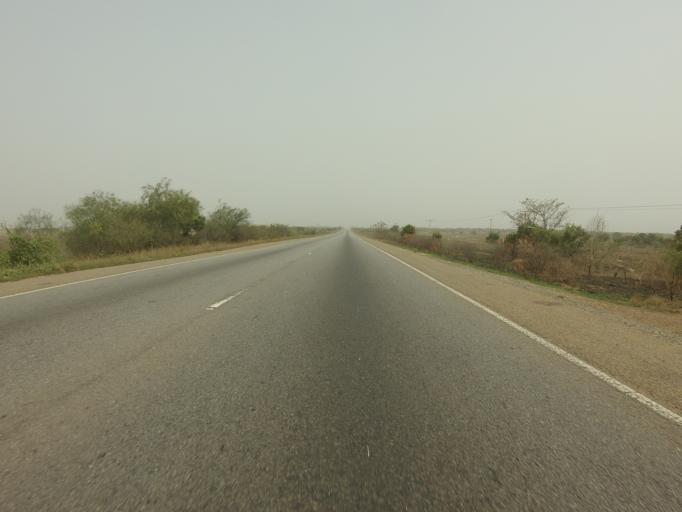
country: GH
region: Greater Accra
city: Tema
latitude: 5.8679
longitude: 0.3050
